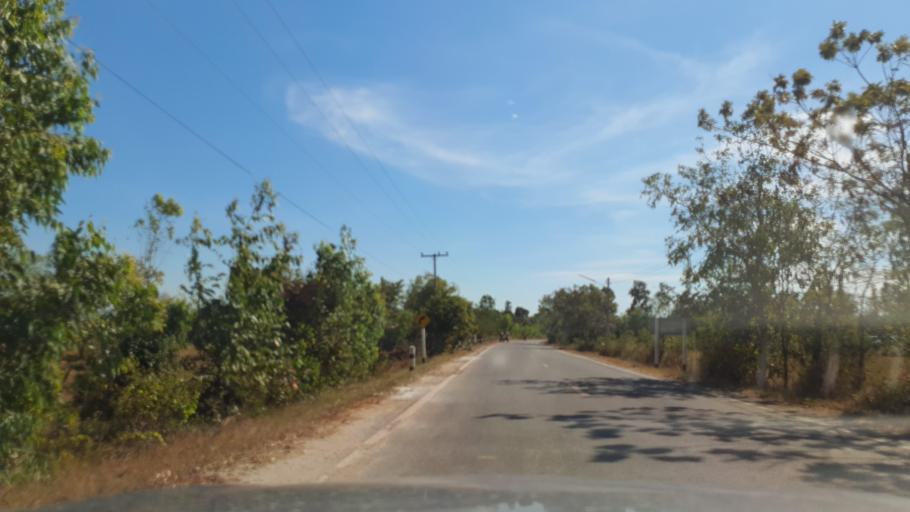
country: TH
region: Kalasin
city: Khao Wong
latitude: 16.7123
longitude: 104.1146
